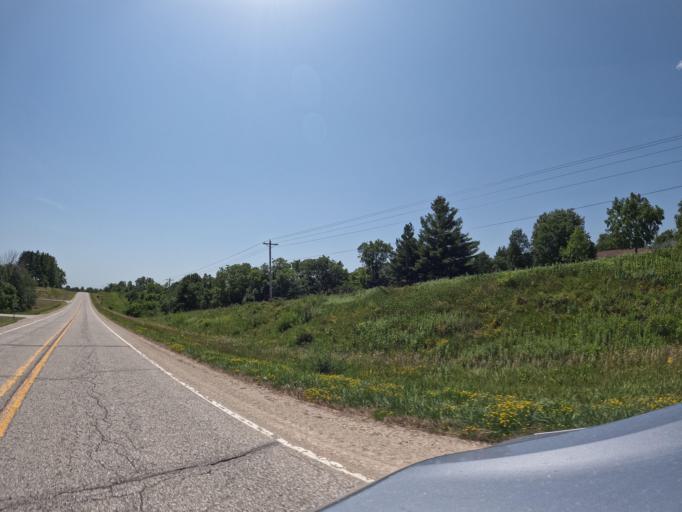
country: US
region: Iowa
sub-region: Henry County
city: Mount Pleasant
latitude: 40.9520
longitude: -91.6125
